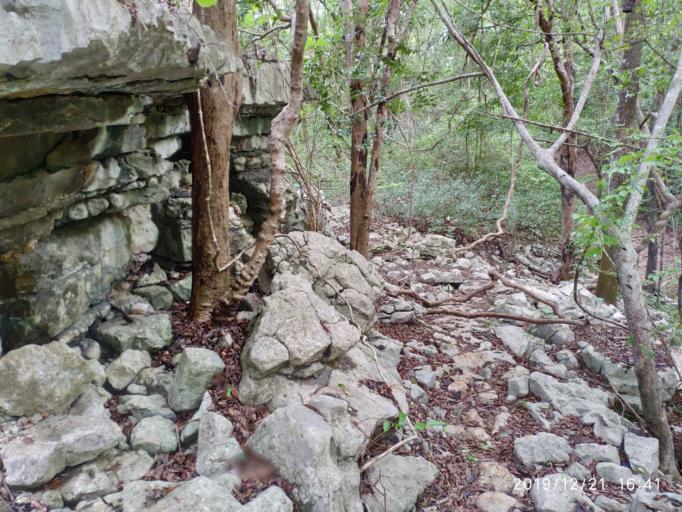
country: MG
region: Diana
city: Ambilobe
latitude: -12.9471
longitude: 49.1256
